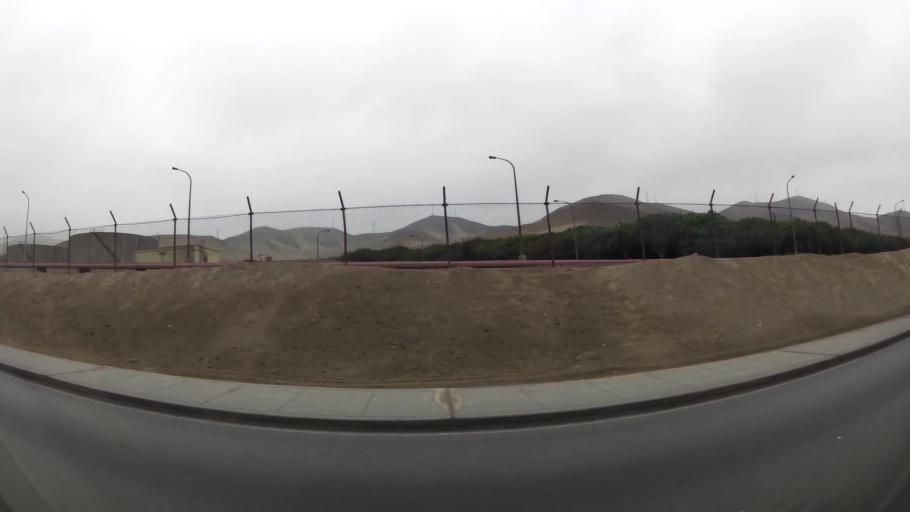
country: PE
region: Lima
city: Ventanilla
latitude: -11.9173
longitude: -77.1286
